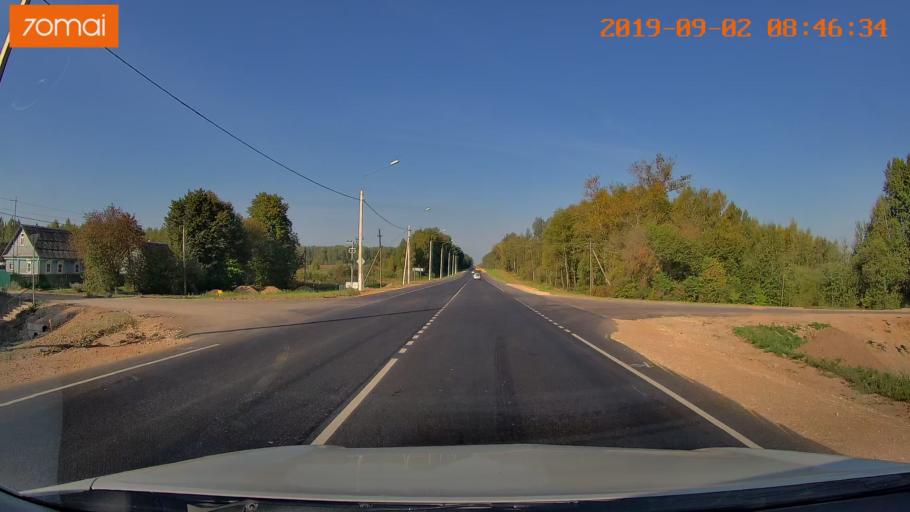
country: RU
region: Kaluga
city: Medyn'
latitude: 54.9686
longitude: 35.9751
